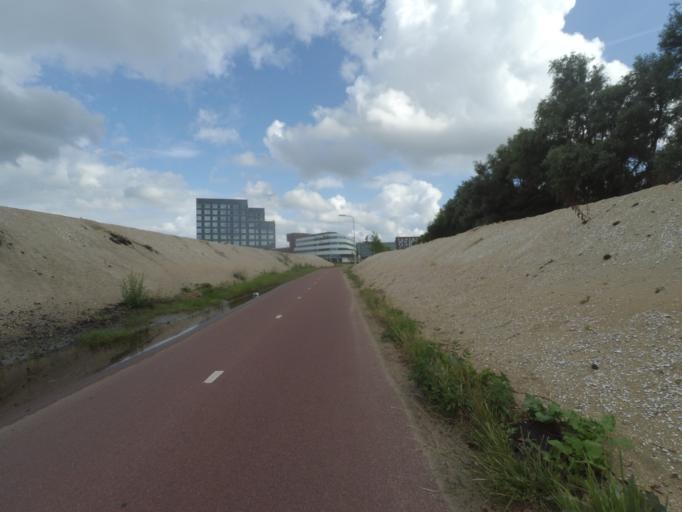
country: NL
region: South Holland
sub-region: Gemeente Den Haag
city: Ypenburg
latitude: 52.0569
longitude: 4.3855
